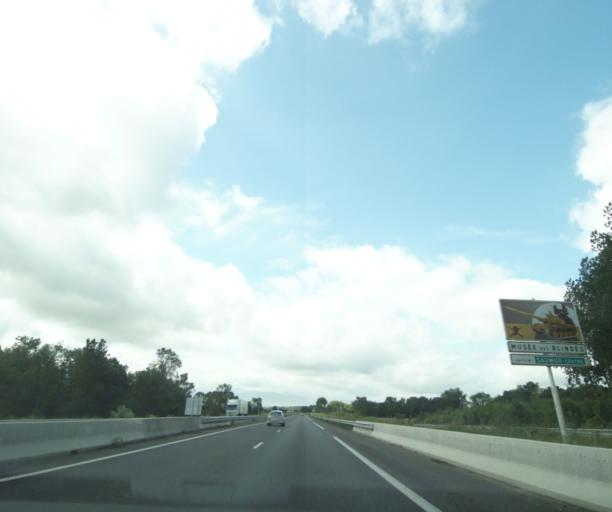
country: FR
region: Pays de la Loire
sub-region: Departement de Maine-et-Loire
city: Vivy
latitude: 47.2935
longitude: -0.0418
